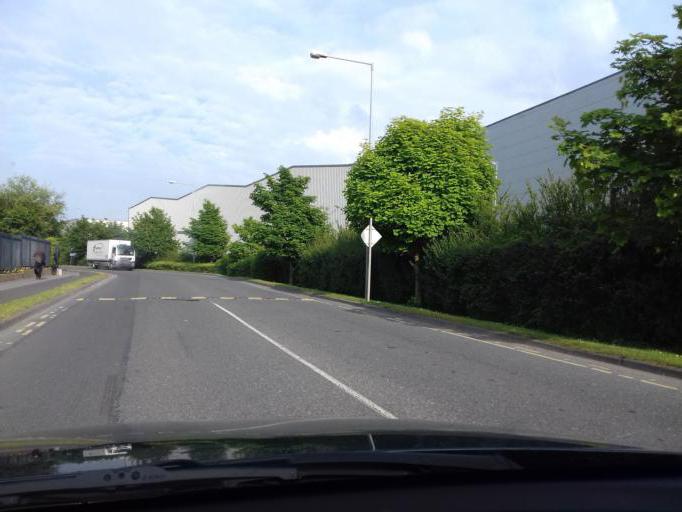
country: IE
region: Leinster
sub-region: Fingal County
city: Blanchardstown
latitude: 53.4107
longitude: -6.3517
